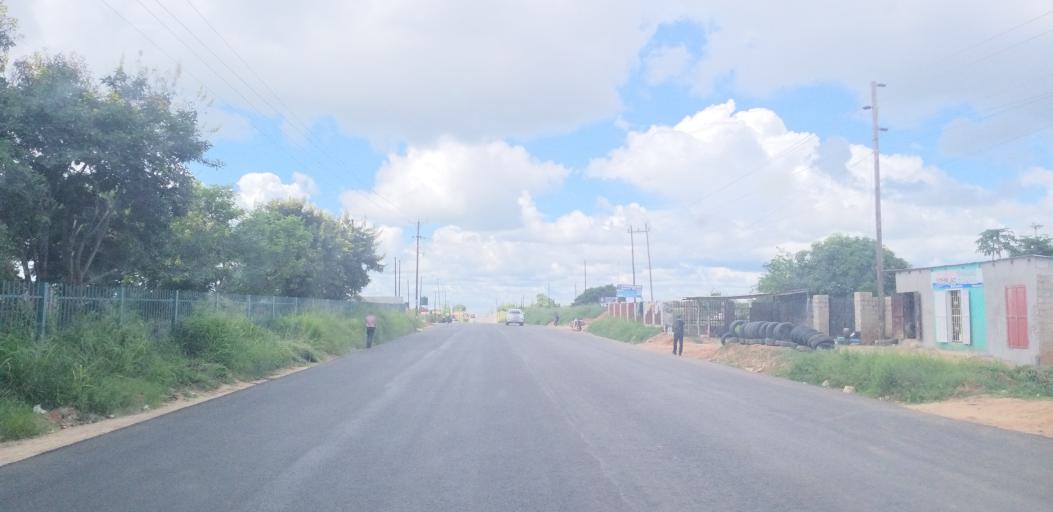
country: ZM
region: Lusaka
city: Lusaka
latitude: -15.3560
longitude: 28.3236
